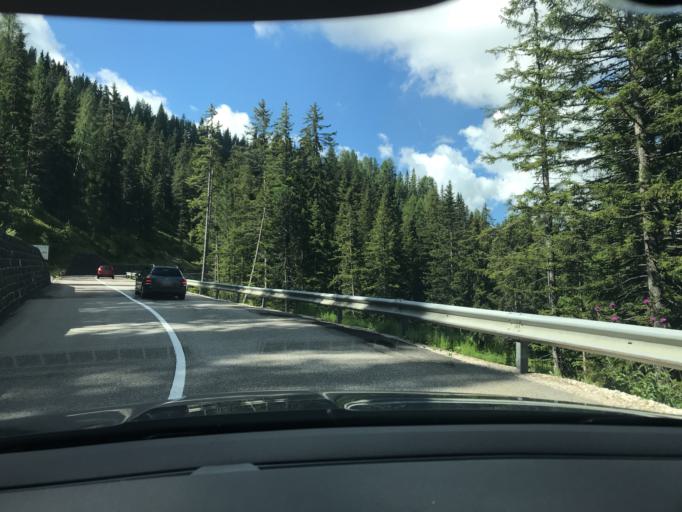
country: IT
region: Veneto
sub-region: Provincia di Belluno
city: Livinallongo del Col di Lana
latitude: 46.5491
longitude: 11.9772
